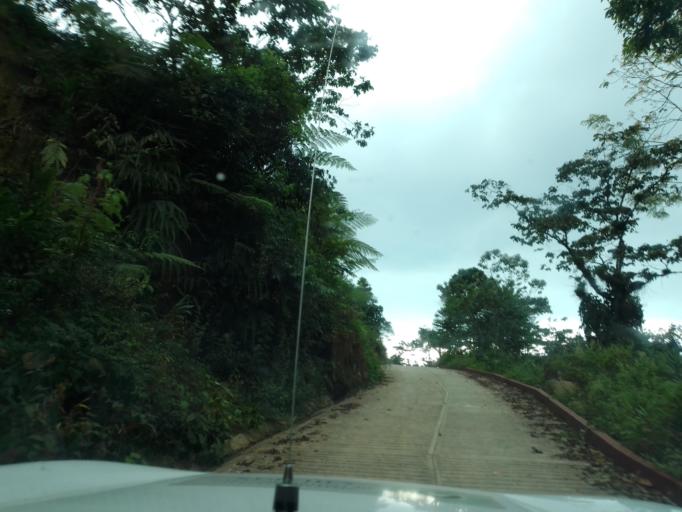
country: MX
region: Chiapas
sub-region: Union Juarez
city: Santo Domingo
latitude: 15.0695
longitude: -92.1159
